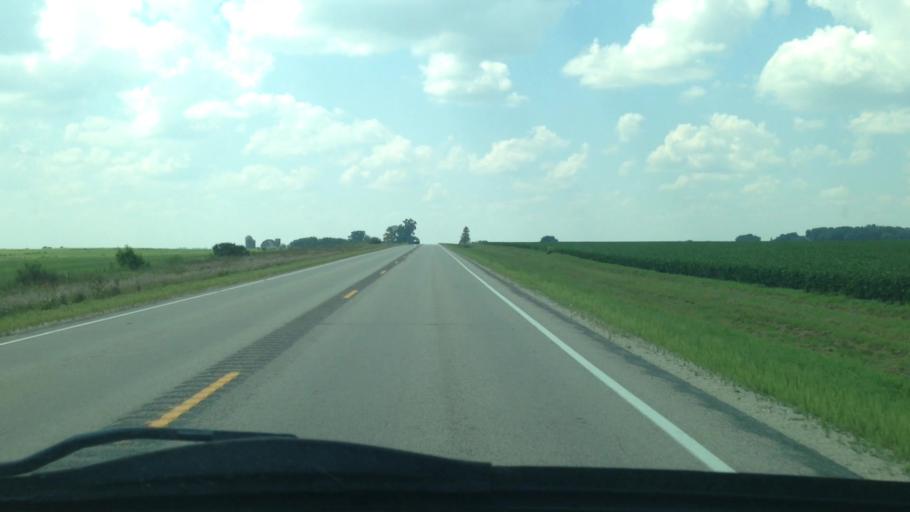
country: US
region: Minnesota
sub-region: Olmsted County
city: Stewartville
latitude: 43.8554
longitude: -92.4210
